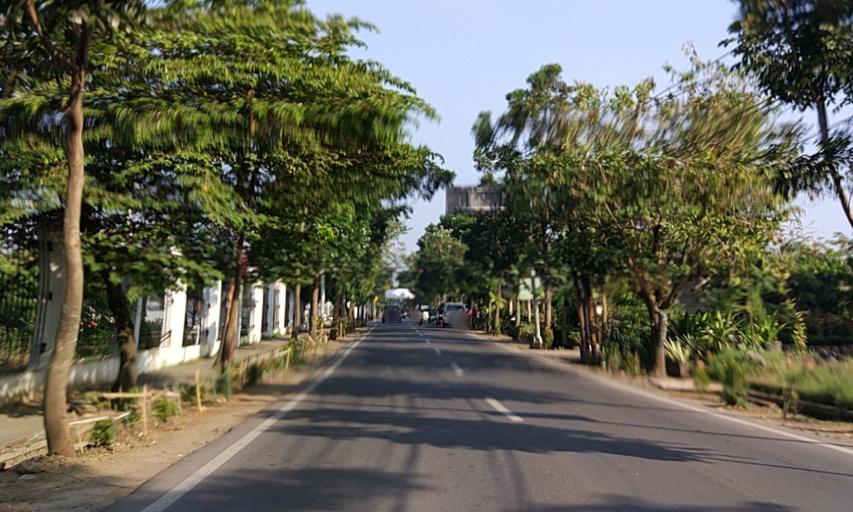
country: ID
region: West Java
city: Bandung
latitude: -6.9101
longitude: 107.6762
